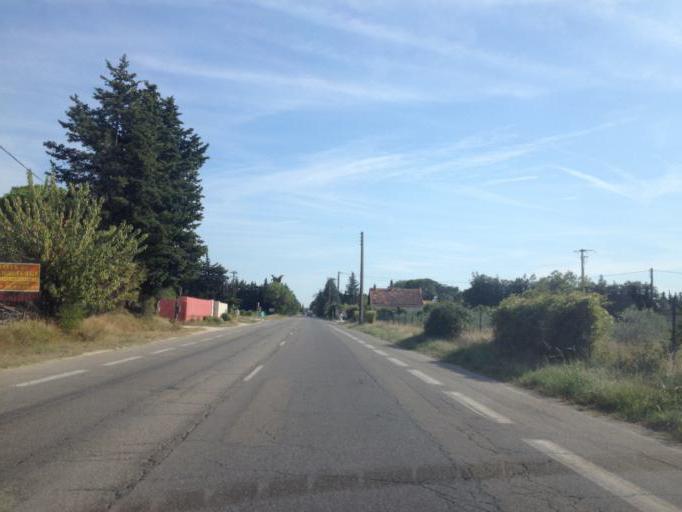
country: FR
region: Provence-Alpes-Cote d'Azur
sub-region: Departement du Vaucluse
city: Carpentras
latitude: 44.0757
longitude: 5.0409
